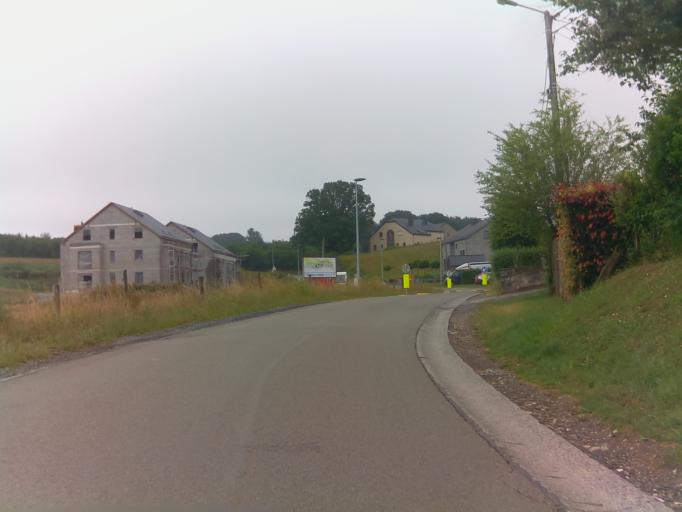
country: BE
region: Wallonia
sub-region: Province du Luxembourg
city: Leglise
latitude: 49.7994
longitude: 5.5391
